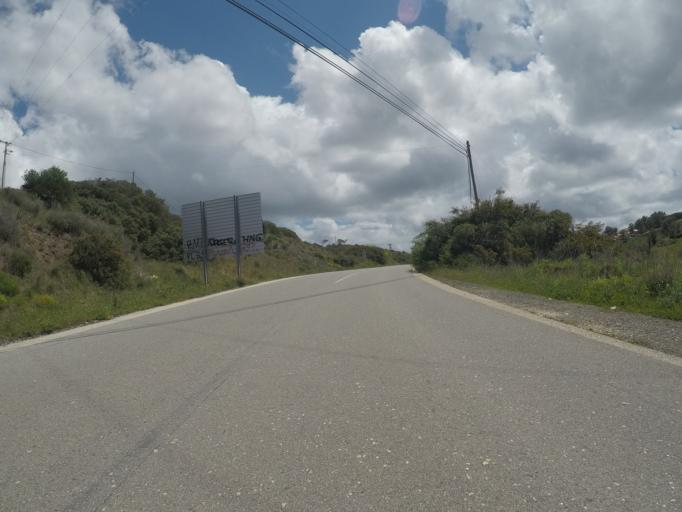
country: PT
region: Faro
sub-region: Vila do Bispo
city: Vila do Bispo
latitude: 37.0782
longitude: -8.8346
